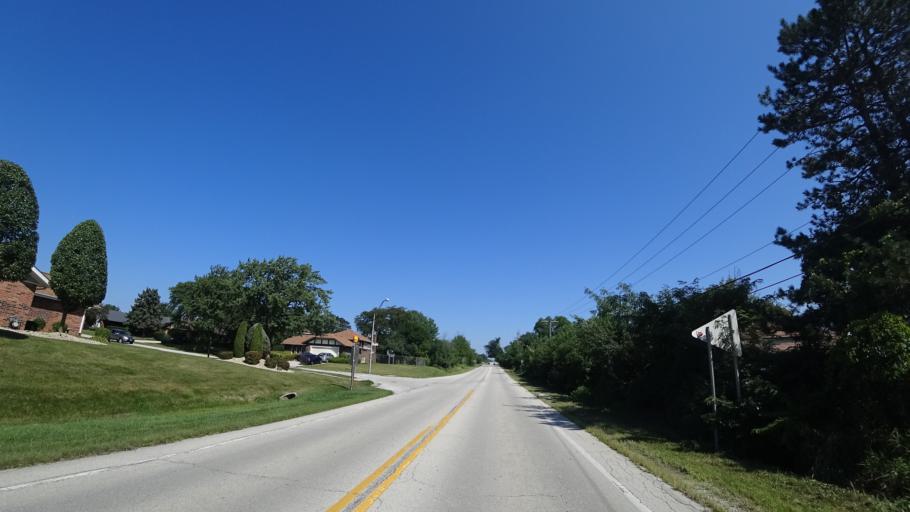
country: US
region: Illinois
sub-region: Cook County
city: Orland Park
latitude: 41.6342
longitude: -87.8198
